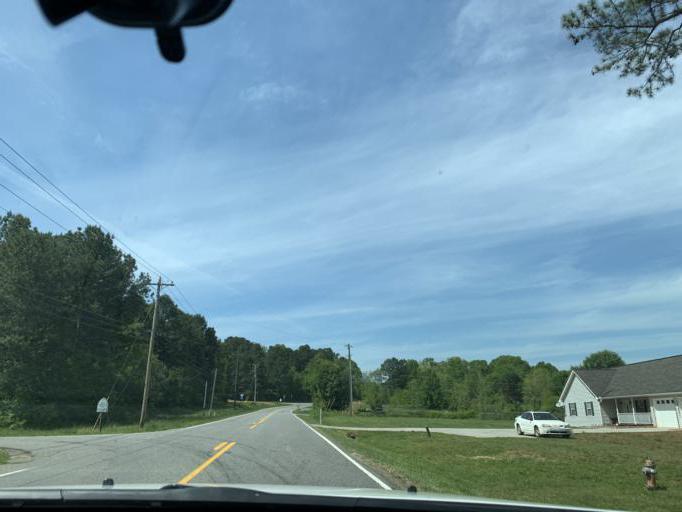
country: US
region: Georgia
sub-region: Forsyth County
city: Cumming
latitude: 34.2662
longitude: -84.1744
